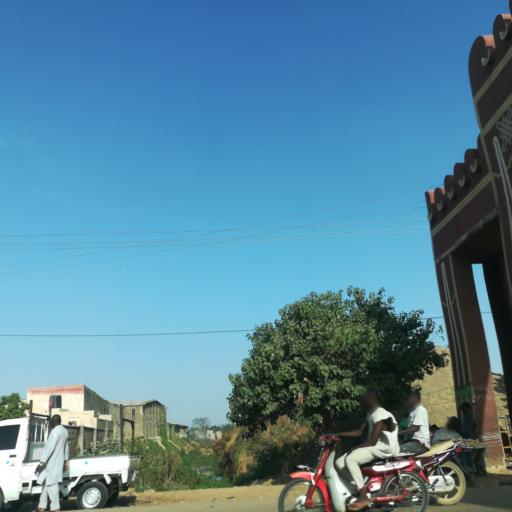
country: NG
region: Kano
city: Kano
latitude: 12.0267
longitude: 8.5008
